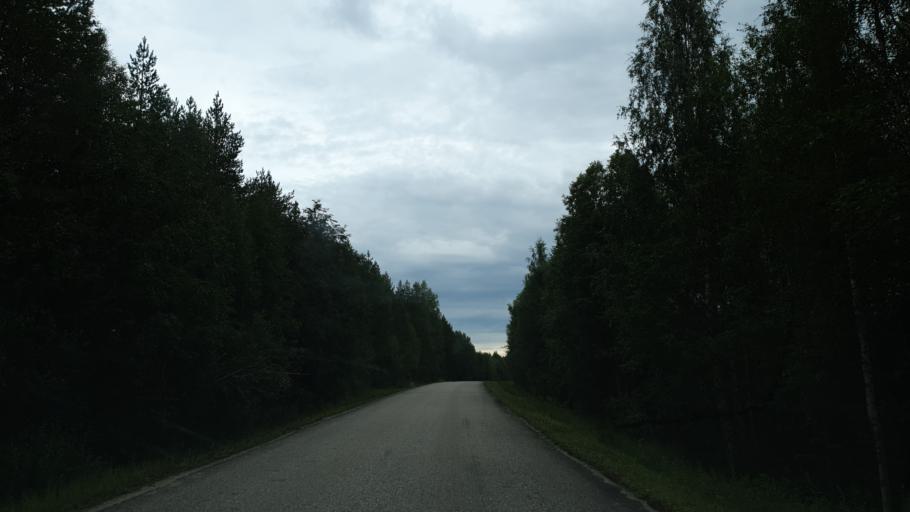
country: FI
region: Kainuu
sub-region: Kehys-Kainuu
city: Kuhmo
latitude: 64.3532
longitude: 29.0780
